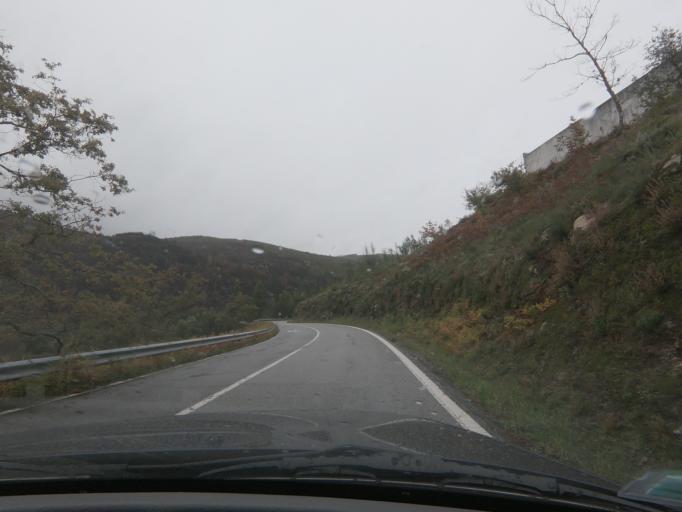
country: PT
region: Vila Real
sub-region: Mondim de Basto
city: Mondim de Basto
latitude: 41.3691
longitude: -7.9276
